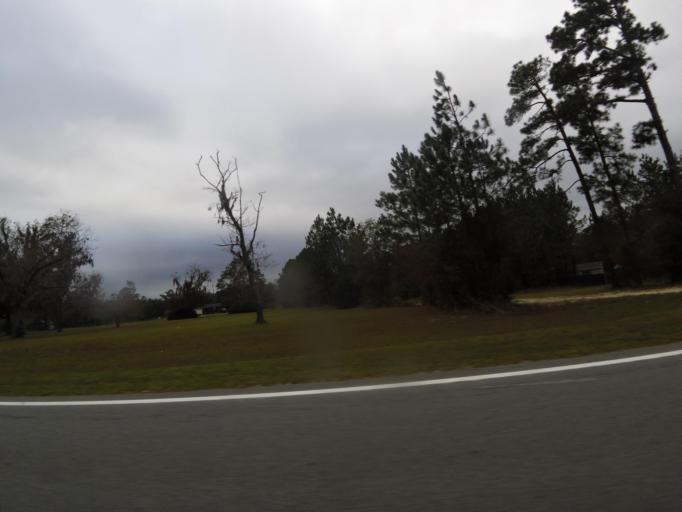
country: US
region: Georgia
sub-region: Charlton County
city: Folkston
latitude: 30.7602
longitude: -82.0698
